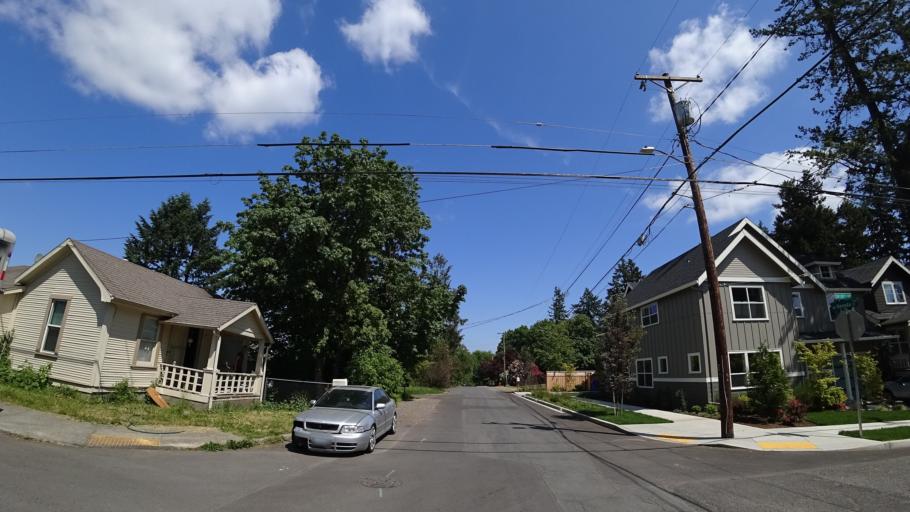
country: US
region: Oregon
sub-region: Washington County
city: Garden Home-Whitford
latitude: 45.4725
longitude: -122.7057
